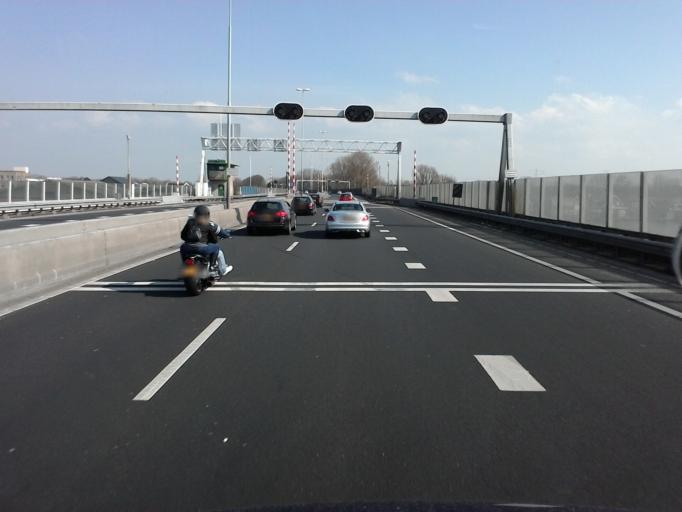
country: NL
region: North Holland
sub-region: Gemeente Zaanstad
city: Zaanstad
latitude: 52.4632
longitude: 4.8112
